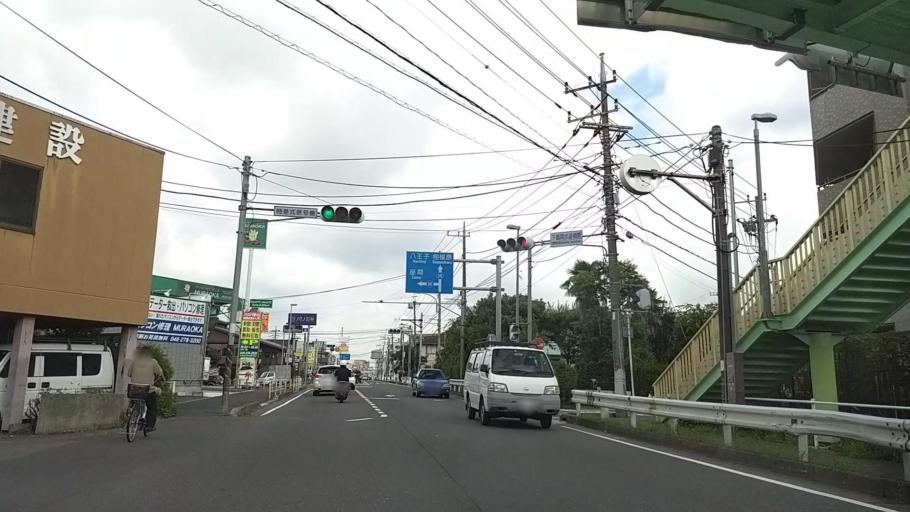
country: JP
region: Kanagawa
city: Minami-rinkan
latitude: 35.5040
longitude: 139.4649
